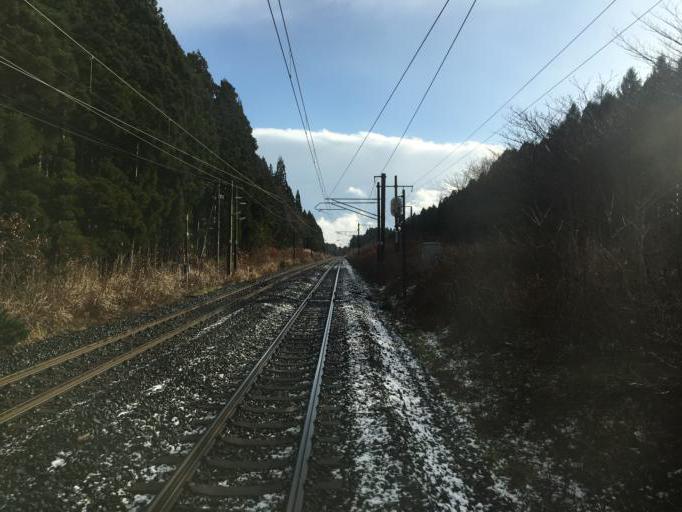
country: JP
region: Aomori
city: Aomori Shi
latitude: 40.9098
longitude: 141.0523
